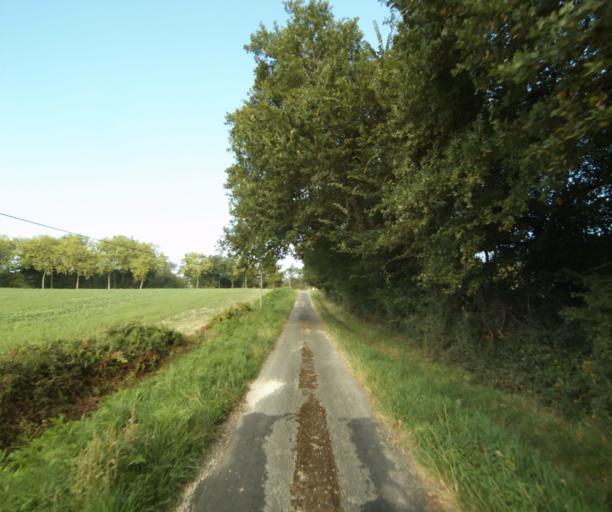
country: FR
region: Midi-Pyrenees
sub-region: Departement du Gers
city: Eauze
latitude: 43.8974
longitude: 0.0337
